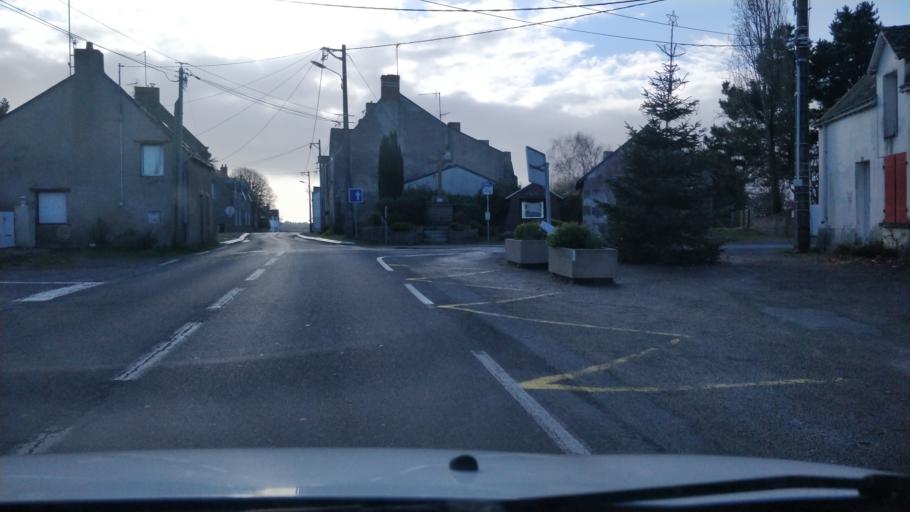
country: FR
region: Pays de la Loire
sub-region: Departement de la Loire-Atlantique
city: Asserac
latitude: 47.4151
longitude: -2.4002
